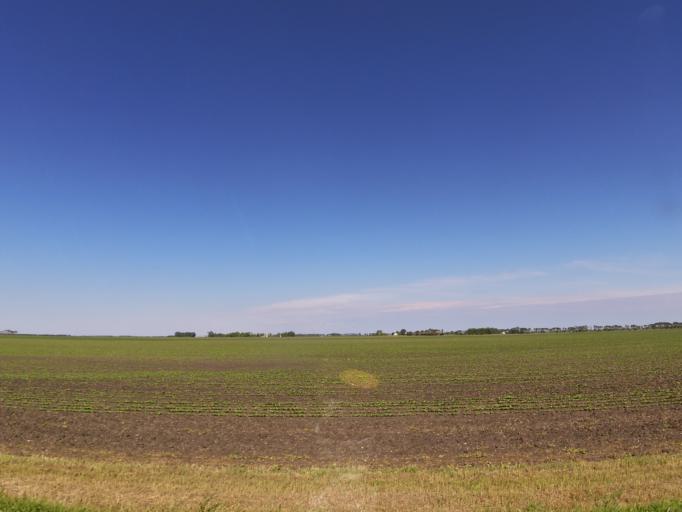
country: US
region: North Dakota
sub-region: Walsh County
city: Grafton
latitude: 48.3475
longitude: -97.2558
